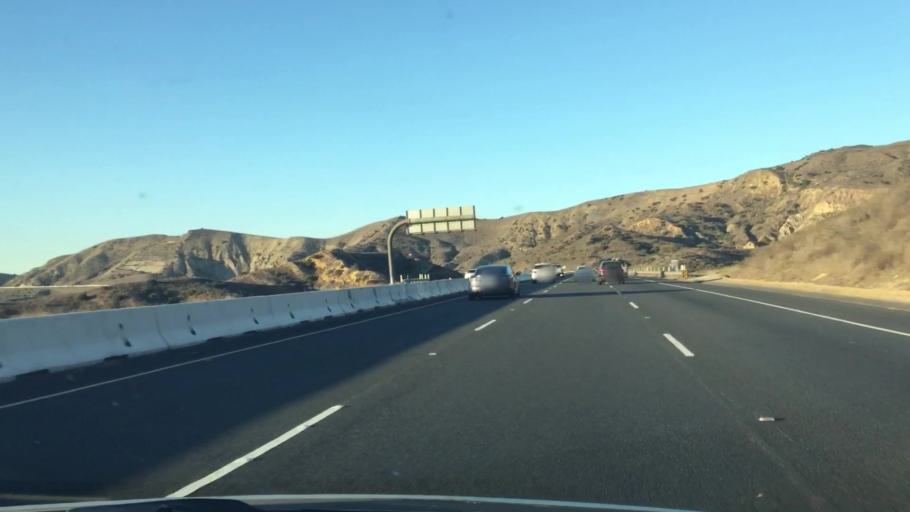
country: US
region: California
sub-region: Orange County
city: Foothill Ranch
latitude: 33.7326
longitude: -117.7181
